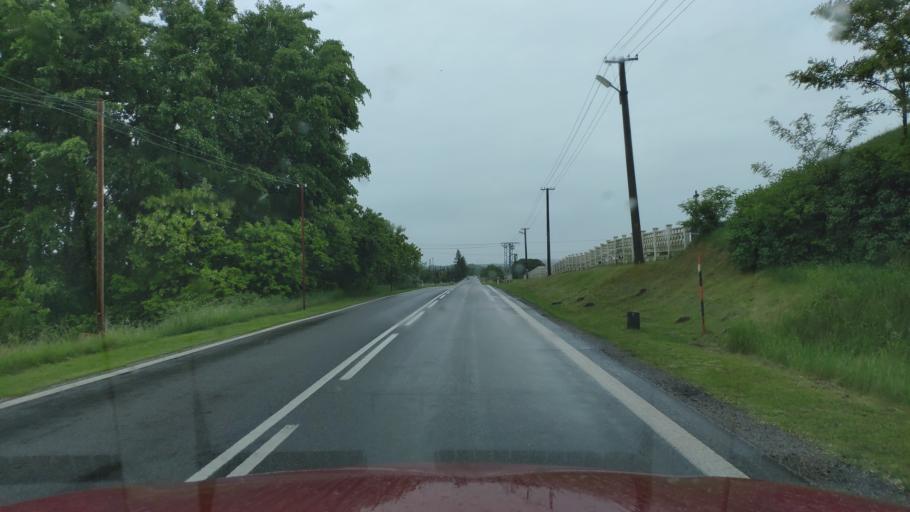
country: HU
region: Borsod-Abauj-Zemplen
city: Karcsa
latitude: 48.4351
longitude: 21.8628
